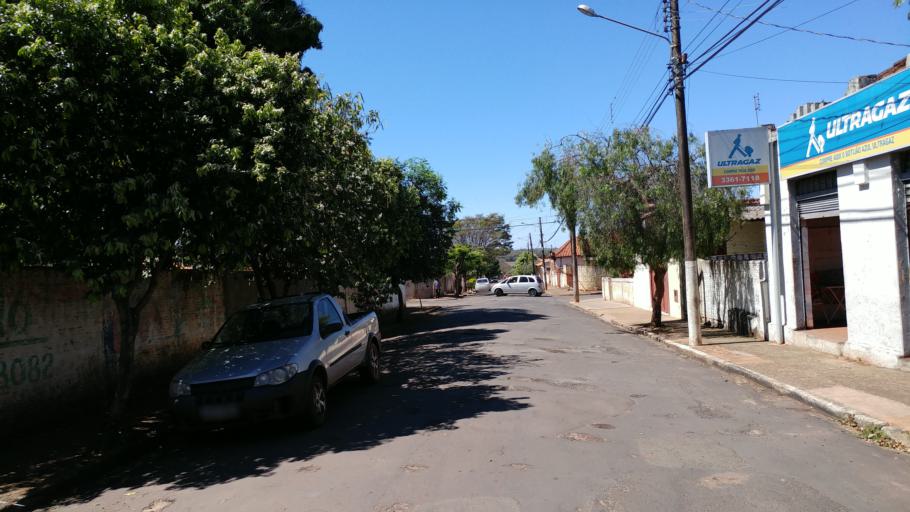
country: BR
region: Sao Paulo
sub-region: Paraguacu Paulista
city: Paraguacu Paulista
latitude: -22.4126
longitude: -50.5703
